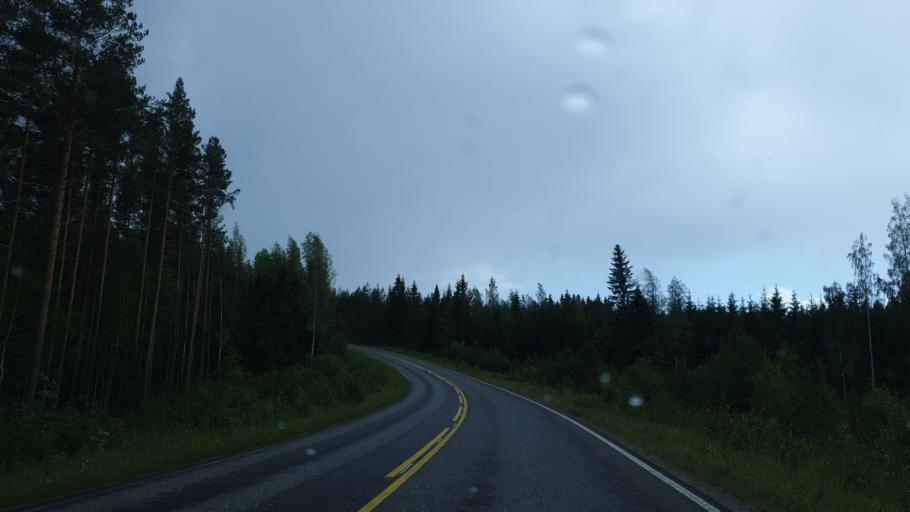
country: FI
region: Northern Savo
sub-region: Kuopio
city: Vehmersalmi
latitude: 62.9332
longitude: 27.9117
